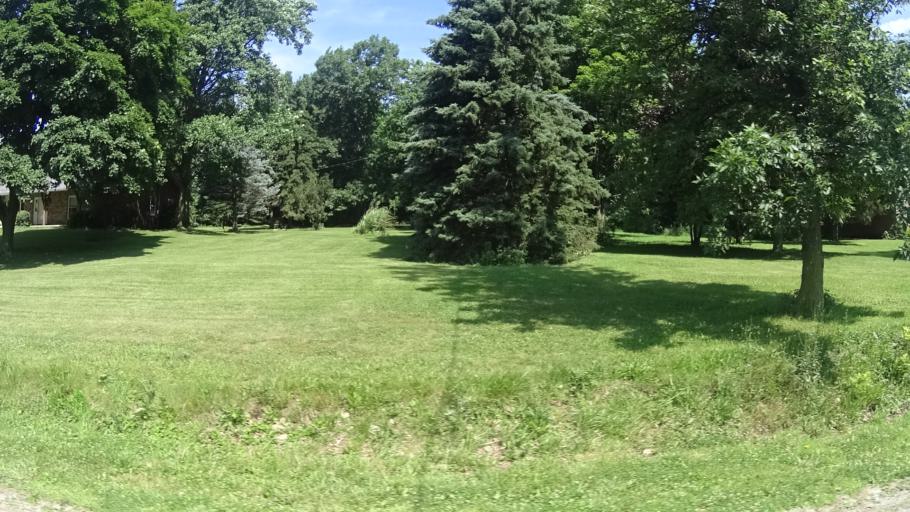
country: US
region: Ohio
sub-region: Huron County
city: Wakeman
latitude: 41.3405
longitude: -82.4404
